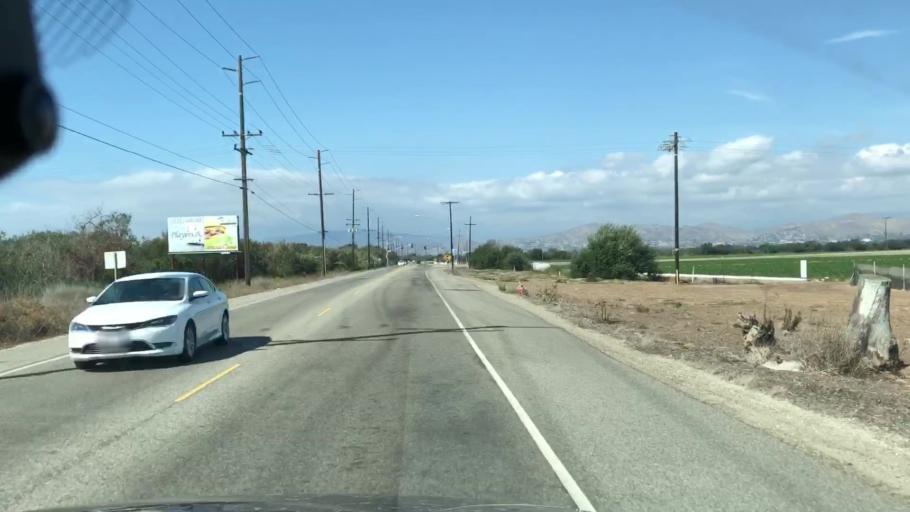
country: US
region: California
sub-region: Ventura County
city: Oxnard Shores
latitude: 34.2161
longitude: -119.2524
